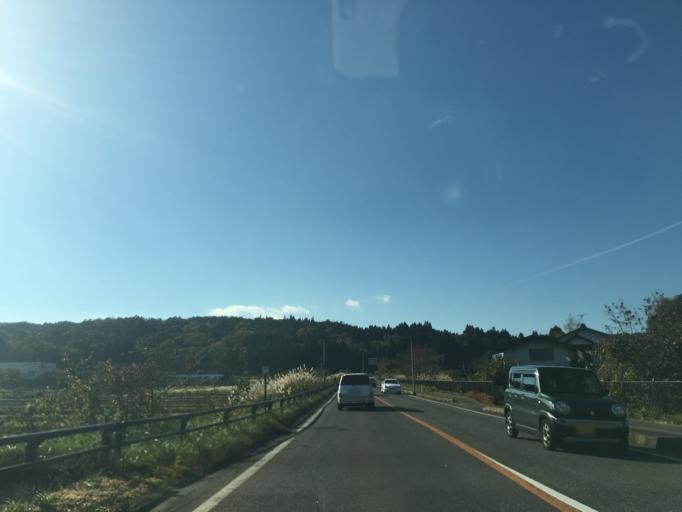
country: JP
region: Fukushima
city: Kitakata
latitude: 37.5707
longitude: 139.8053
